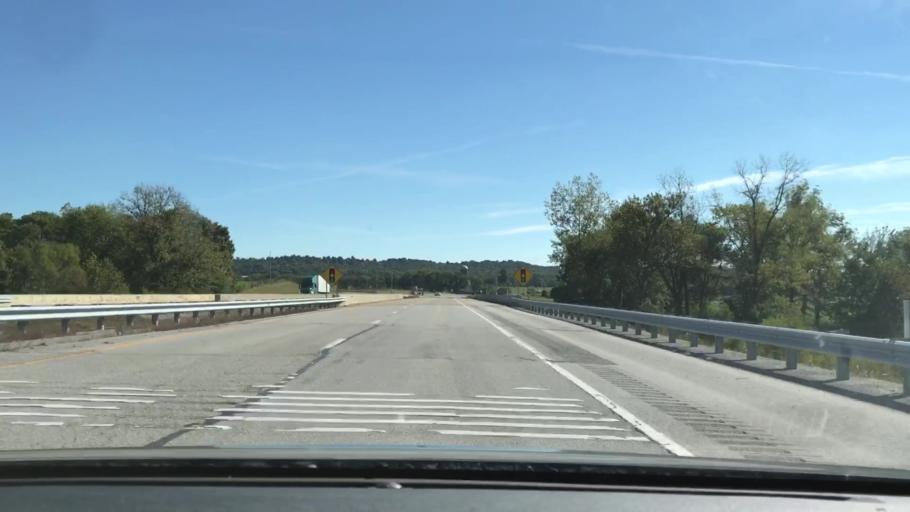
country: US
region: Kentucky
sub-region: Todd County
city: Elkton
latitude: 36.8245
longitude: -87.1555
